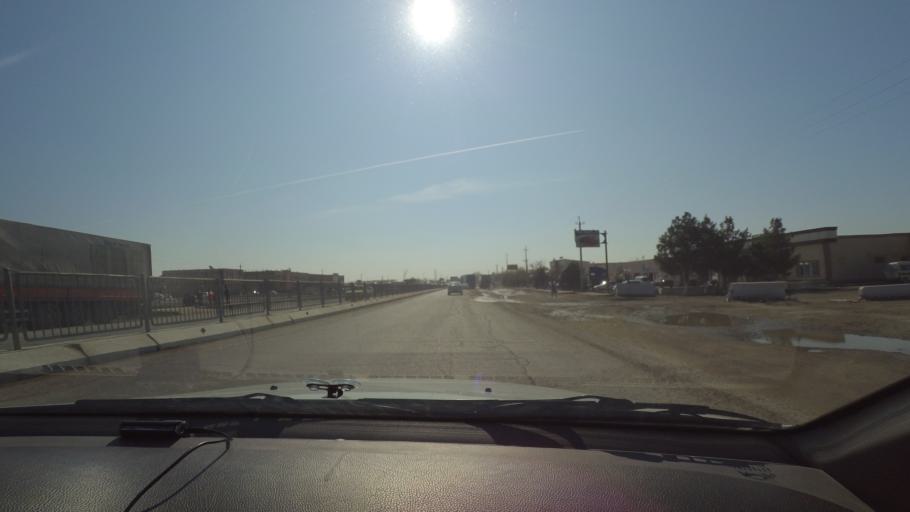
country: UZ
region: Bukhara
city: Bukhara
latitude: 39.8073
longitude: 64.4209
